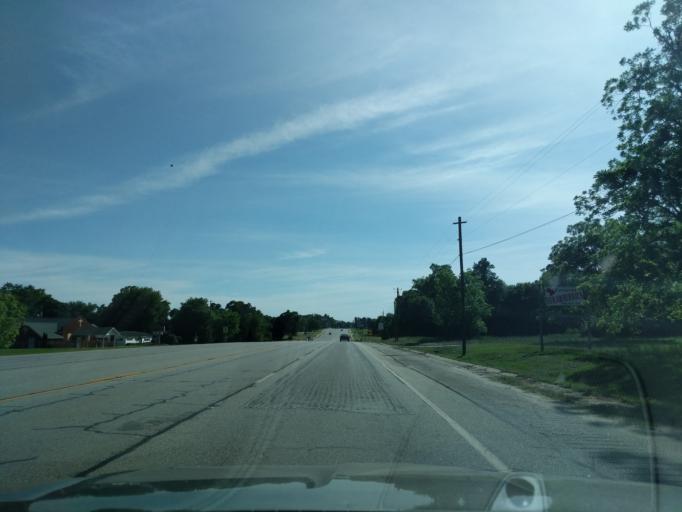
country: US
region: Georgia
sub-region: Jefferson County
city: Wrens
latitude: 33.2223
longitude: -82.3713
